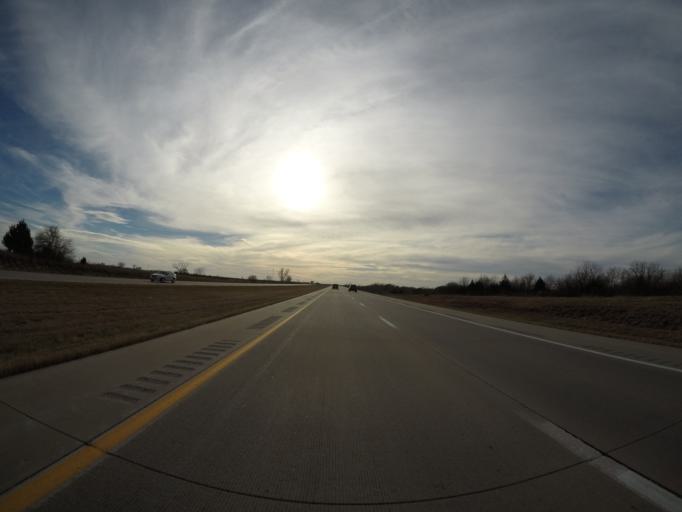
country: US
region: Kansas
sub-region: Johnson County
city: Edgerton
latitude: 38.7266
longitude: -95.0345
